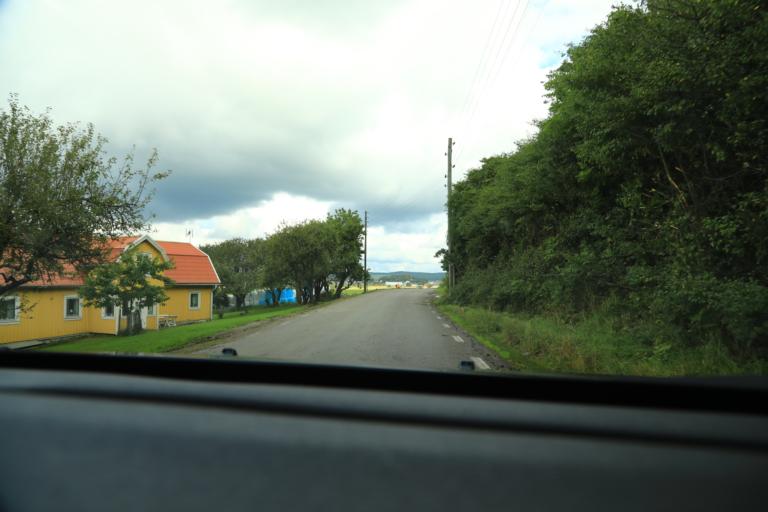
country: SE
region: Halland
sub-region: Kungsbacka Kommun
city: Kungsbacka
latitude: 57.5186
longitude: 12.0950
